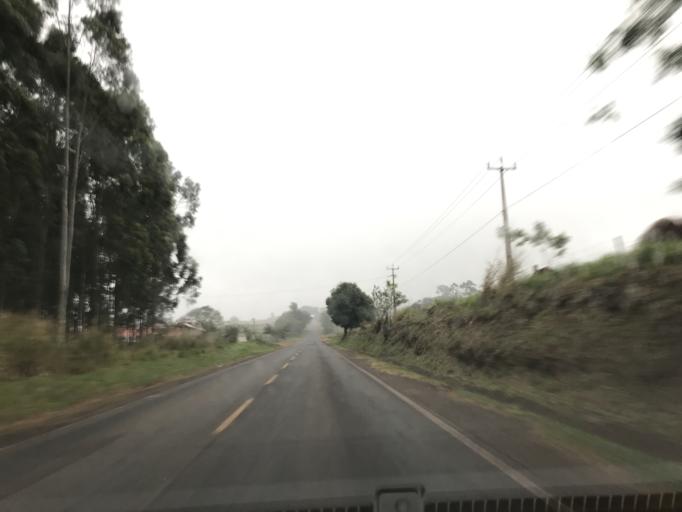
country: PY
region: Canindeyu
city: Salto del Guaira
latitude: -24.1426
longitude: -54.1073
